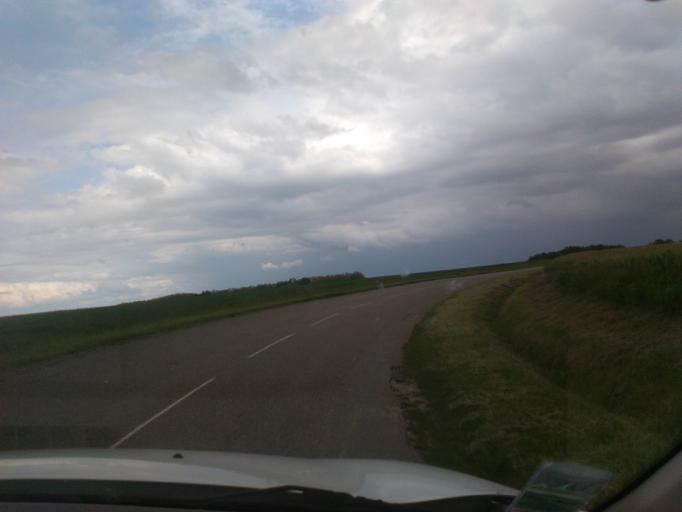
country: FR
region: Bourgogne
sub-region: Departement de l'Yonne
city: Thorigny-sur-Oreuse
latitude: 48.3560
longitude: 3.4212
